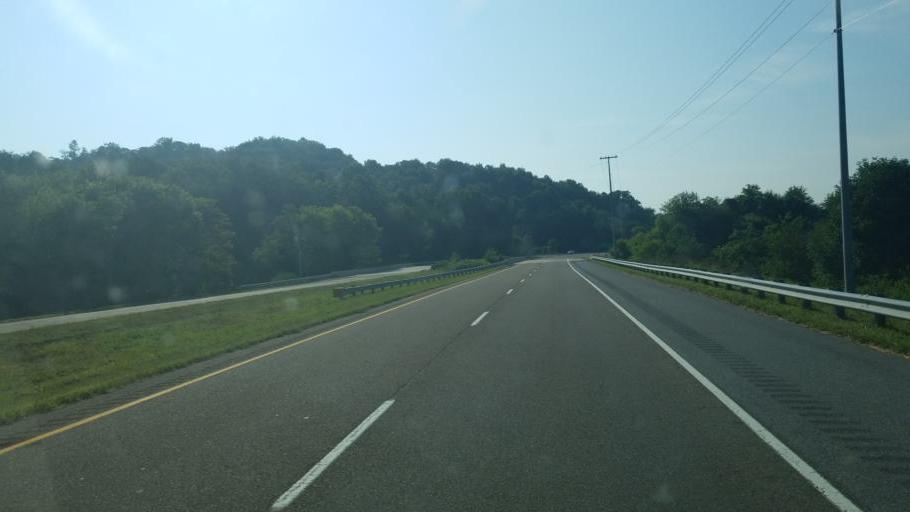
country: US
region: Tennessee
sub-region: Carter County
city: Elizabethton
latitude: 36.3806
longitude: -82.2223
